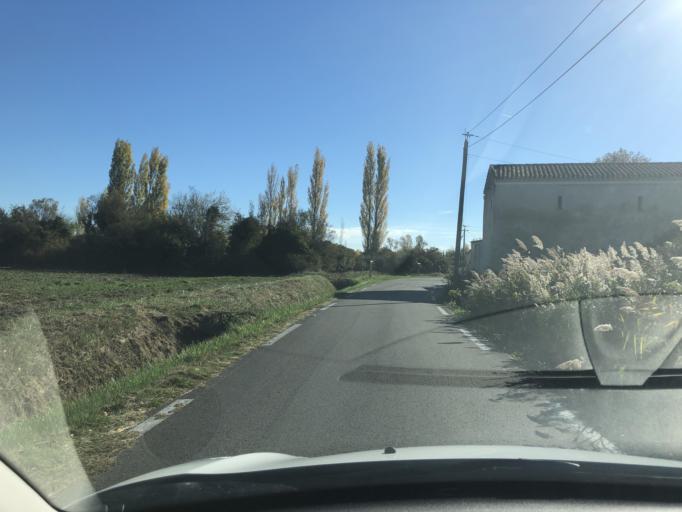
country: FR
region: Provence-Alpes-Cote d'Azur
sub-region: Departement du Vaucluse
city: Entraigues-sur-la-Sorgue
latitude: 43.9855
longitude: 4.9389
